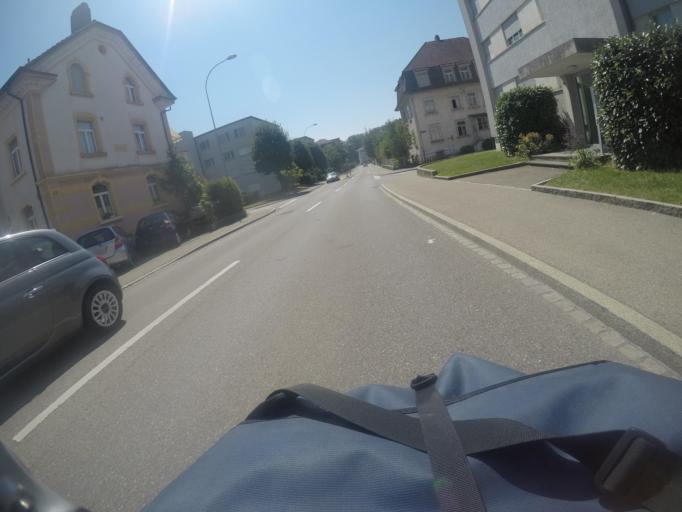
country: CH
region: Thurgau
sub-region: Arbon District
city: Arbon
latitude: 47.5125
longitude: 9.4251
